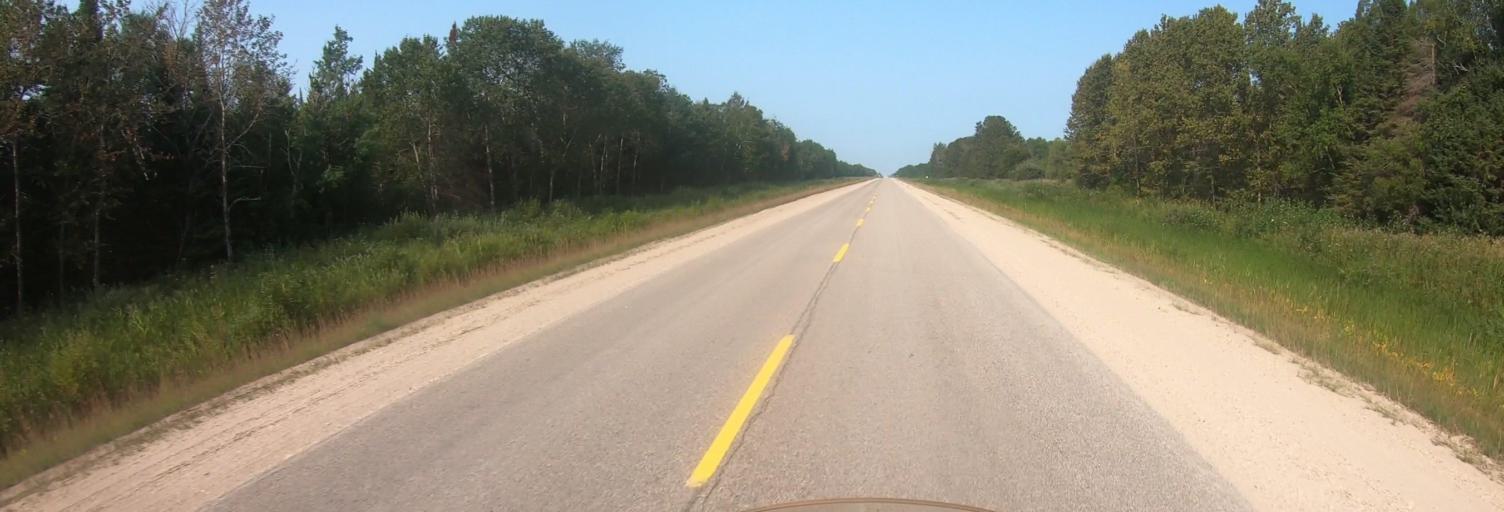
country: US
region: Minnesota
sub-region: Roseau County
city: Warroad
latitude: 49.0163
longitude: -95.4268
